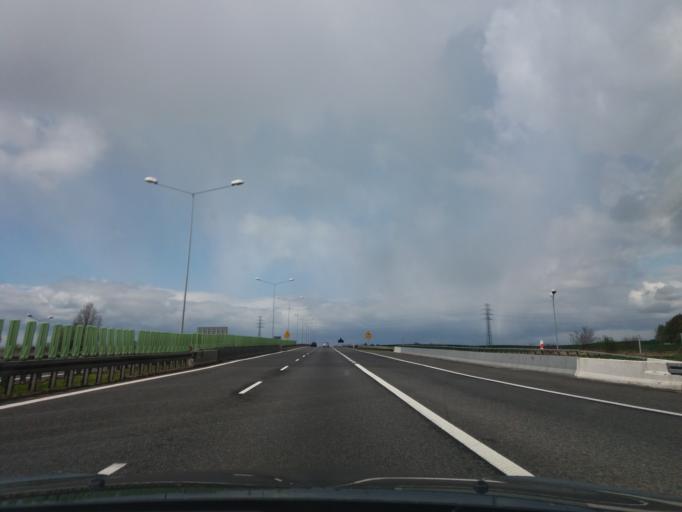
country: PL
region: Silesian Voivodeship
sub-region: Powiat gliwicki
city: Rudziniec
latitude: 50.3932
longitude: 18.4458
